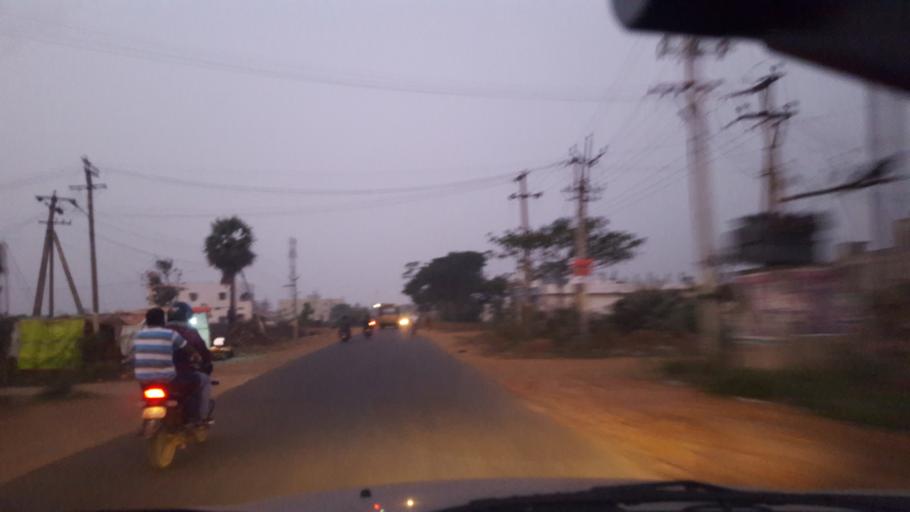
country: IN
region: Andhra Pradesh
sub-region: Srikakulam
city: Palasa
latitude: 18.7504
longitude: 84.4160
